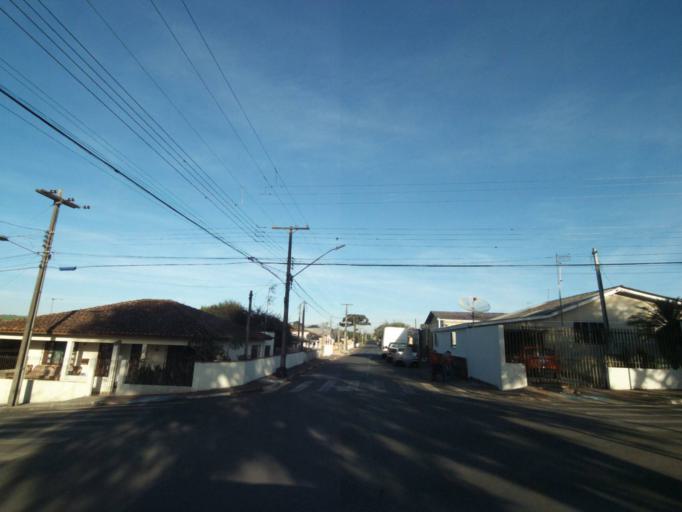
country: BR
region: Parana
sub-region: Tibagi
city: Tibagi
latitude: -24.5212
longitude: -50.4052
